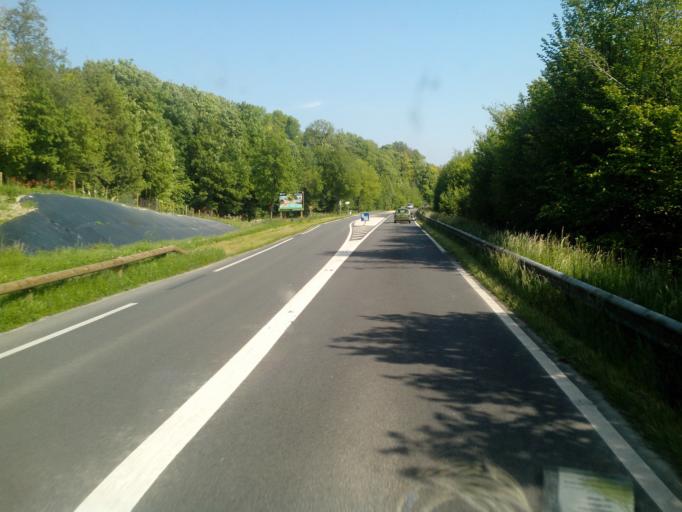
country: FR
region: Picardie
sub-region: Departement de la Somme
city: Sailly-Flibeaucourt
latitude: 50.1410
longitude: 1.7628
